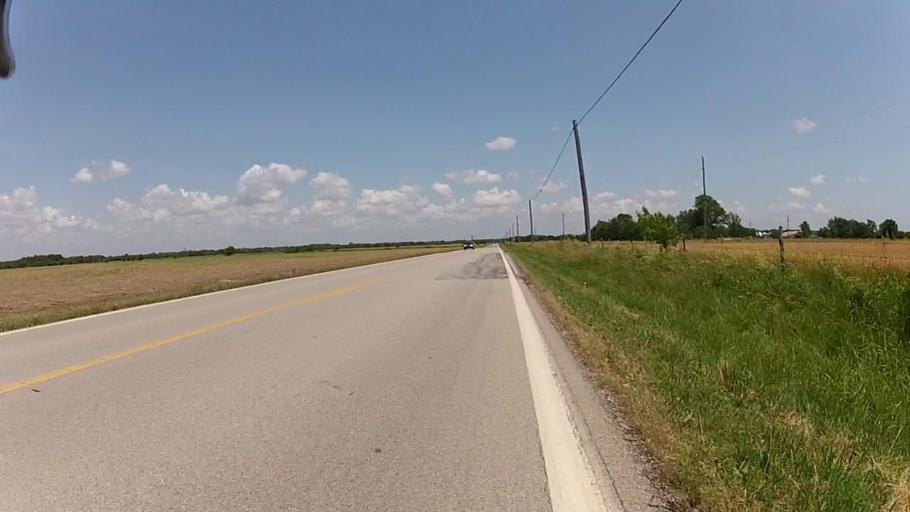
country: US
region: Kansas
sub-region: Labette County
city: Altamont
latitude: 37.1926
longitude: -95.4296
